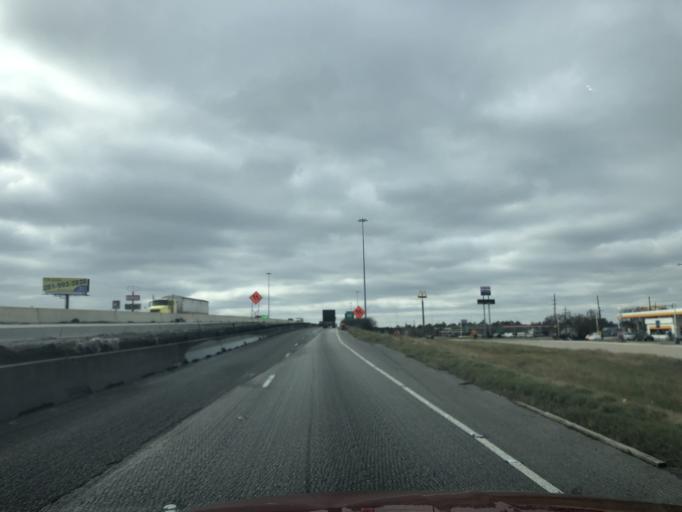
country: US
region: Texas
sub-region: Chambers County
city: Winnie
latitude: 29.8361
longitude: -94.3820
